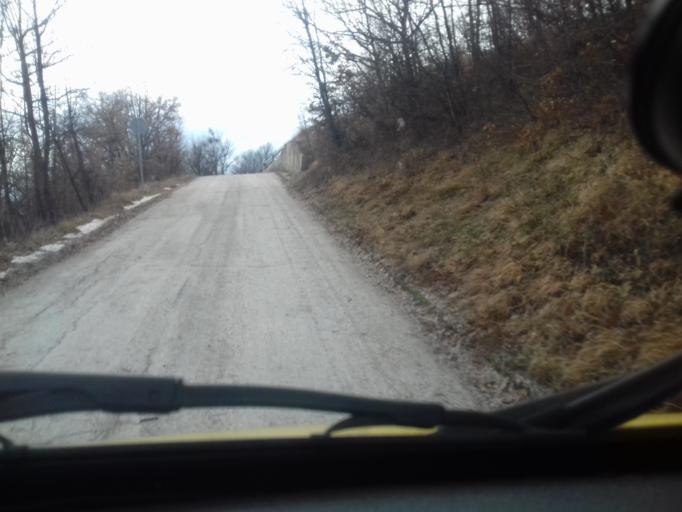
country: BA
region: Federation of Bosnia and Herzegovina
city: Zenica
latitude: 44.2268
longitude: 17.9484
